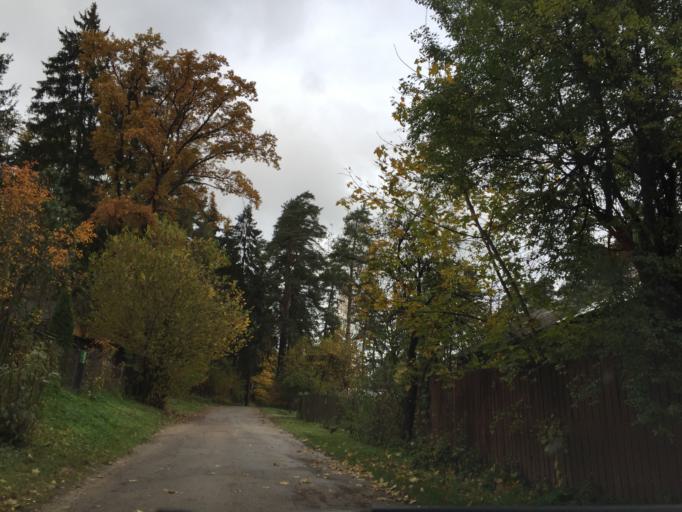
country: LV
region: Ogre
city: Ogre
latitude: 56.8085
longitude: 24.6306
